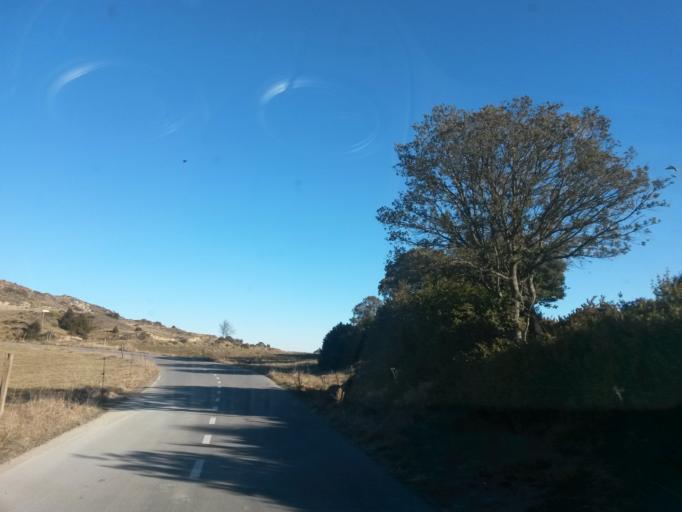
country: ES
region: Catalonia
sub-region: Provincia de Girona
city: les Planes d'Hostoles
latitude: 42.0348
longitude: 2.5223
